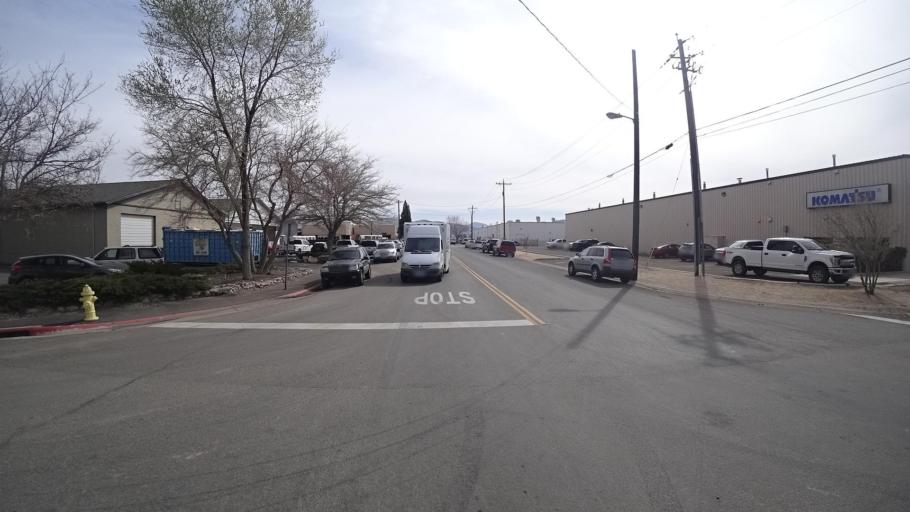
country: US
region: Nevada
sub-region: Washoe County
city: Sparks
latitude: 39.5255
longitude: -119.7539
